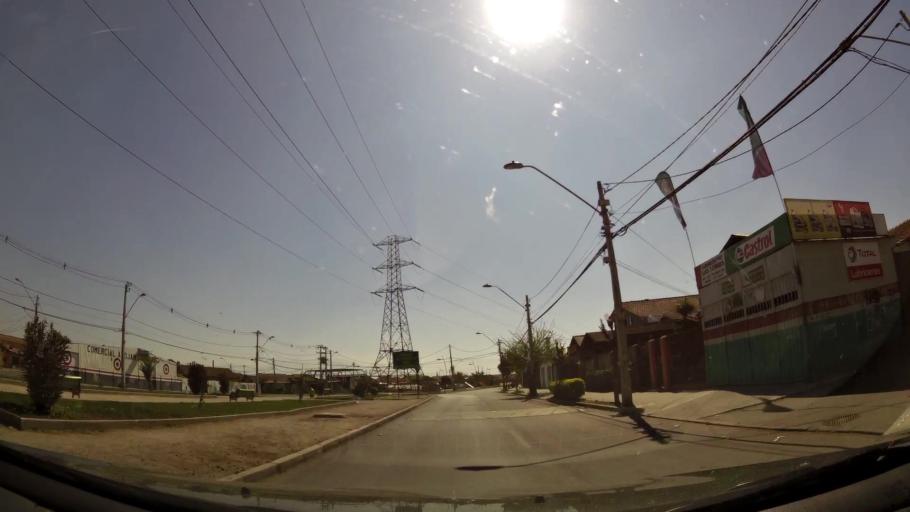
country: CL
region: Santiago Metropolitan
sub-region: Provincia de Santiago
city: Lo Prado
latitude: -33.3494
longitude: -70.7422
